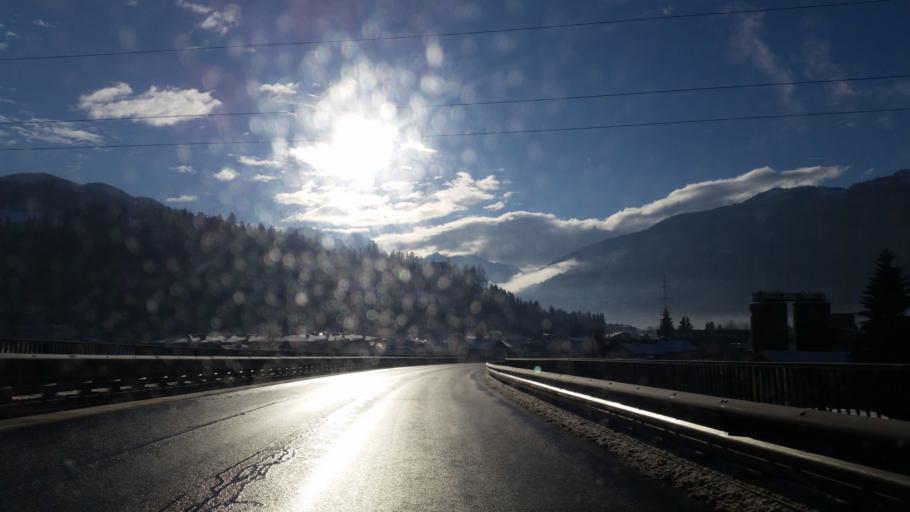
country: AT
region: Salzburg
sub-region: Politischer Bezirk Sankt Johann im Pongau
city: Radstadt
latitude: 47.3846
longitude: 13.4738
